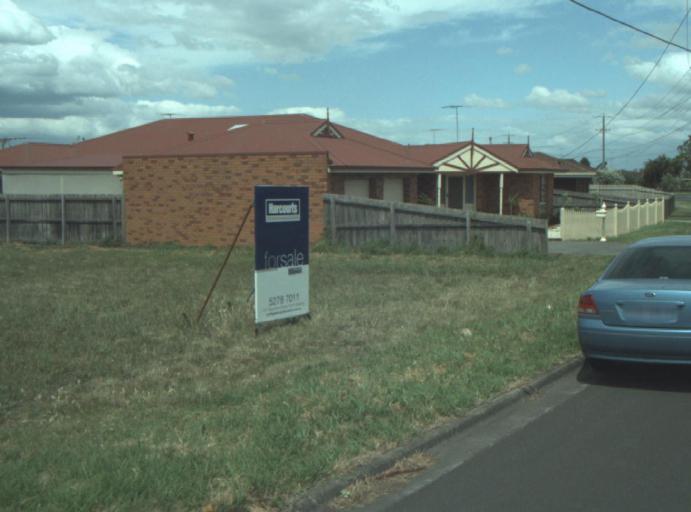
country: AU
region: Victoria
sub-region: Greater Geelong
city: Bell Park
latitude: -38.0891
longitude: 144.3382
